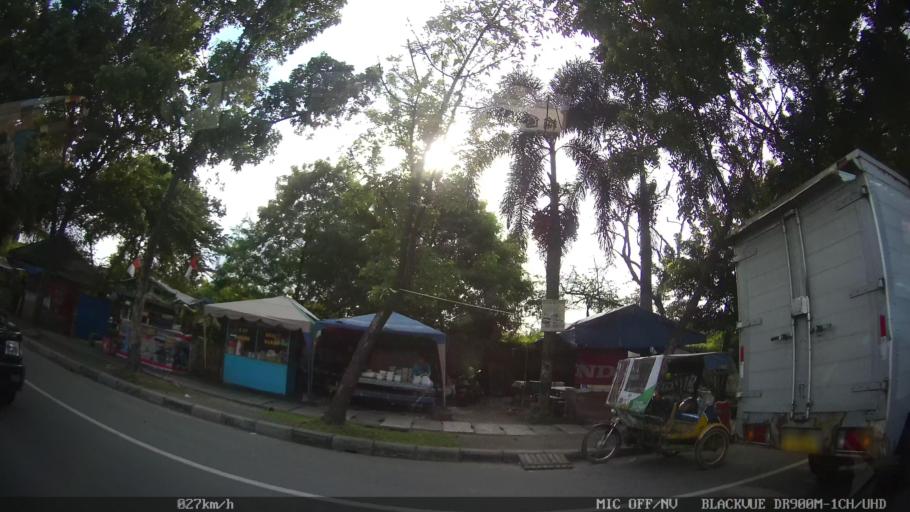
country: ID
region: North Sumatra
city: Medan
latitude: 3.6331
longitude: 98.6811
